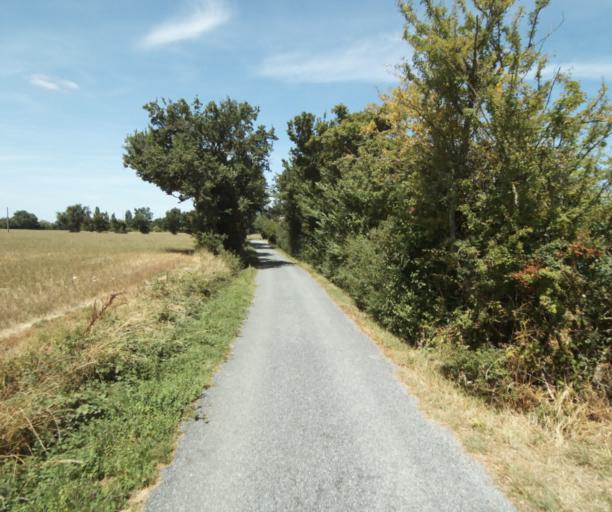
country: FR
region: Midi-Pyrenees
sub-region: Departement du Tarn
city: Soreze
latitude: 43.4894
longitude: 2.0609
